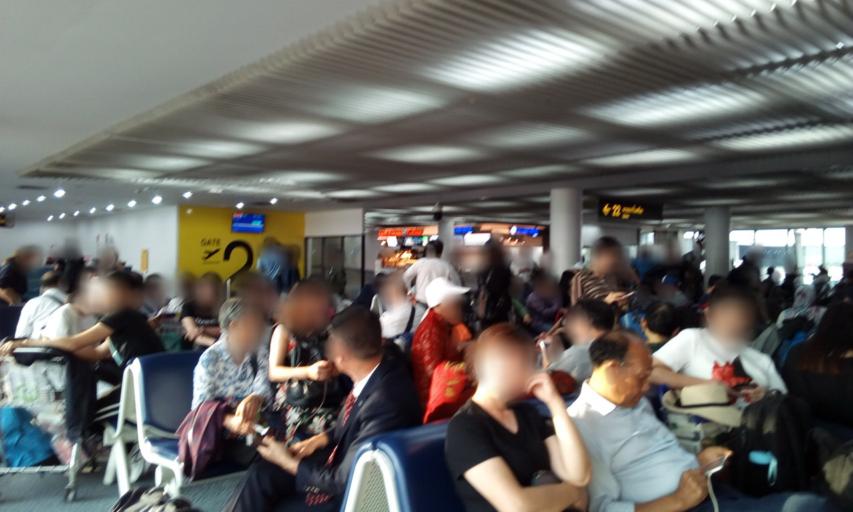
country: TH
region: Bangkok
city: Don Mueang
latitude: 13.9203
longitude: 100.6045
